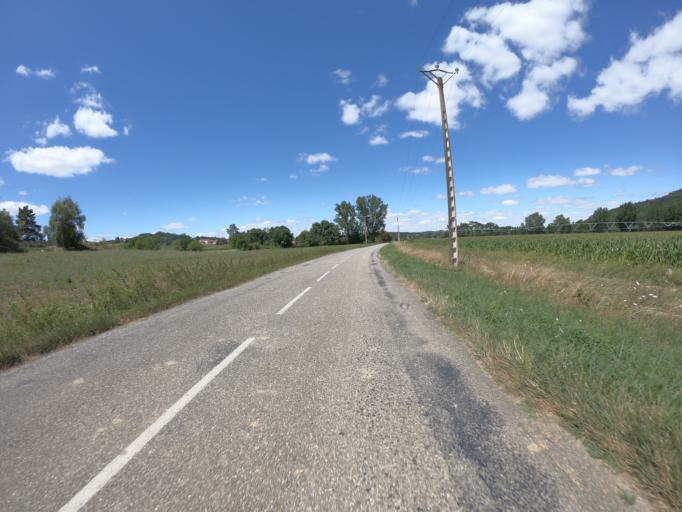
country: FR
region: Midi-Pyrenees
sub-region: Departement de l'Ariege
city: Verniolle
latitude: 43.0580
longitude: 1.7432
